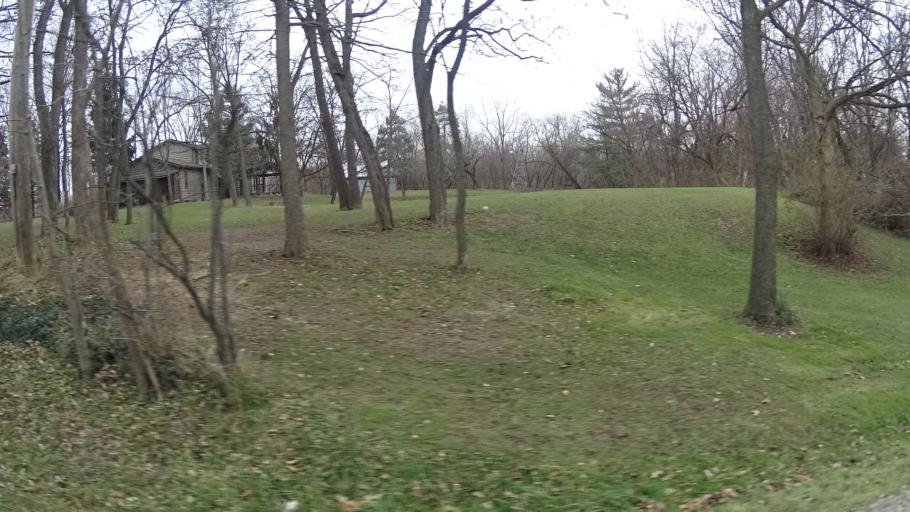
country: US
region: Ohio
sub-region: Medina County
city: Brunswick
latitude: 41.2761
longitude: -81.8780
